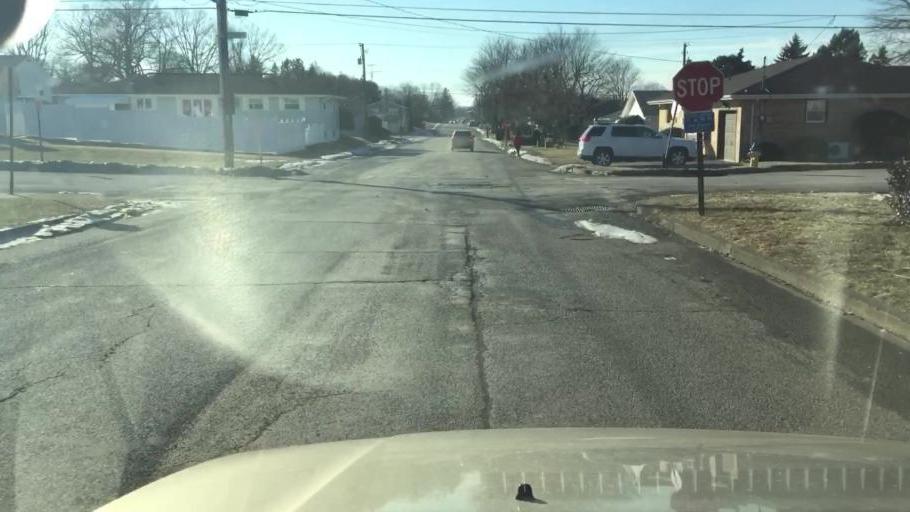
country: US
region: Pennsylvania
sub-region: Luzerne County
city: West Hazleton
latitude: 40.9685
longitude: -75.9887
